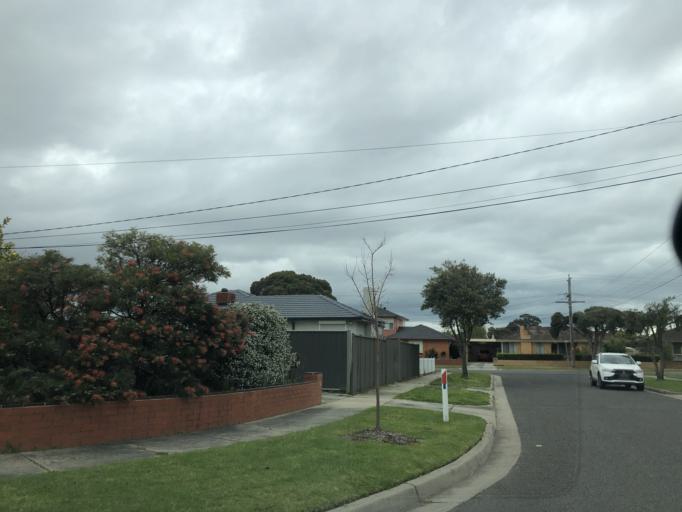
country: AU
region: Victoria
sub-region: Greater Dandenong
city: Dandenong
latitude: -37.9801
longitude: 145.1873
